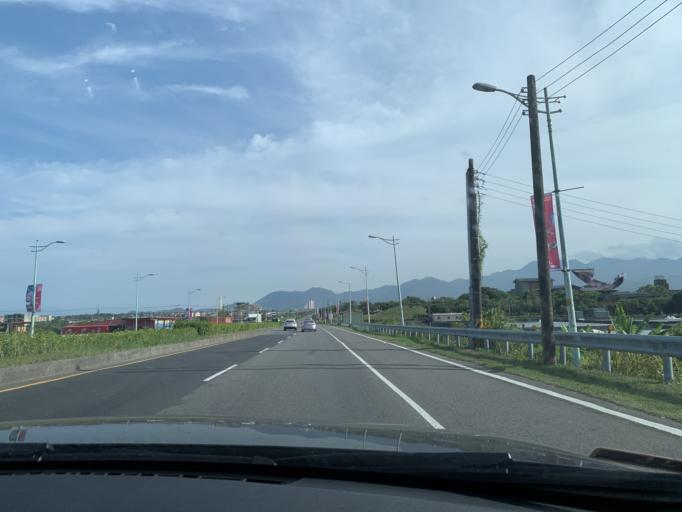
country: TW
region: Taiwan
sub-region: Yilan
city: Yilan
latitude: 24.6908
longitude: 121.8249
